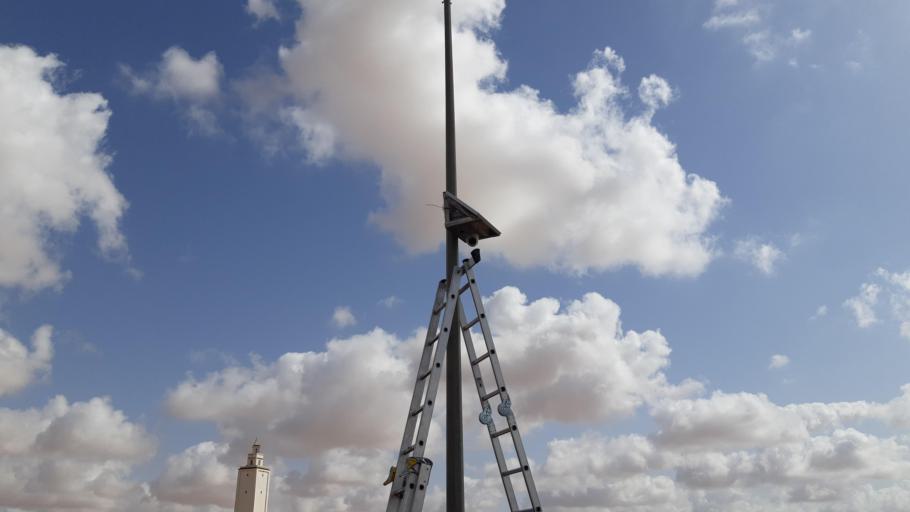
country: TN
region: Safaqis
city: Skhira
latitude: 34.4958
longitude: 10.0540
